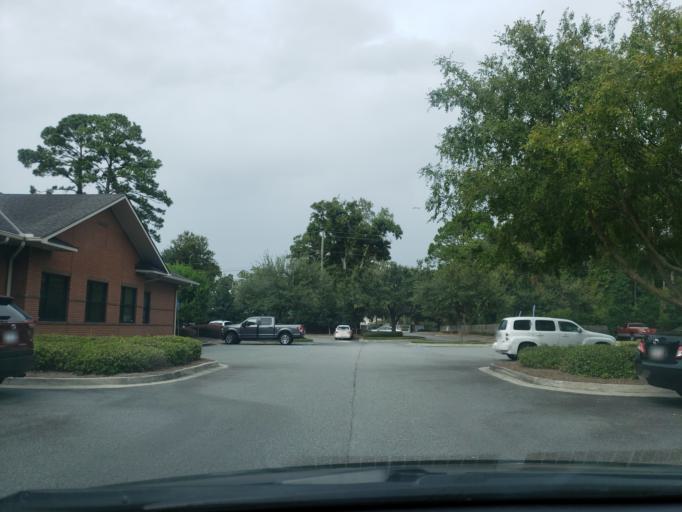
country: US
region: Georgia
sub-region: Chatham County
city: Isle of Hope
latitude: 32.0101
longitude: -81.0985
